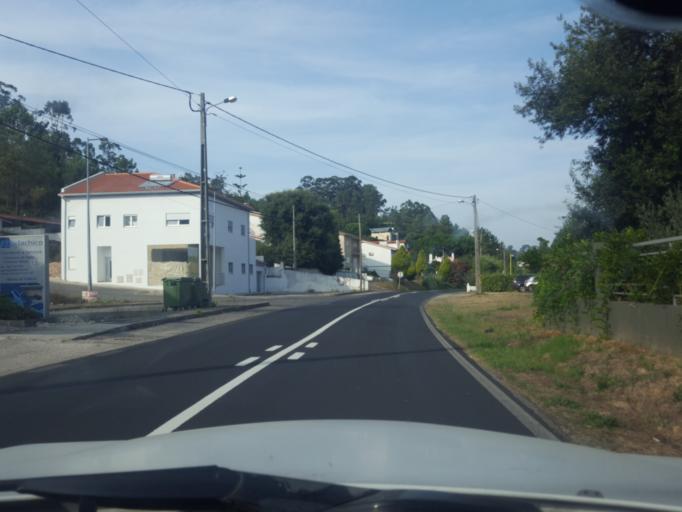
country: PT
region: Leiria
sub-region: Leiria
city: Leiria
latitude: 39.7089
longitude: -8.7926
